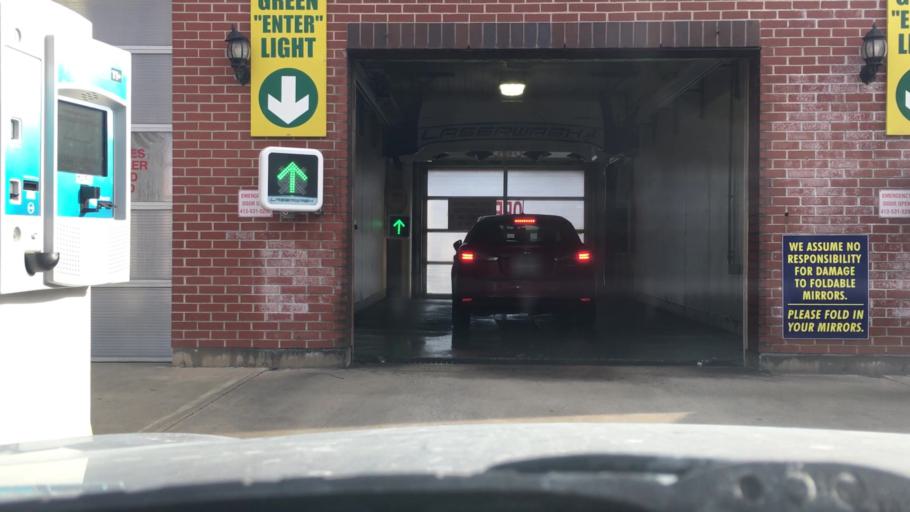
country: US
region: Massachusetts
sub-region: Hampden County
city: Agawam
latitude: 42.0699
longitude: -72.6624
